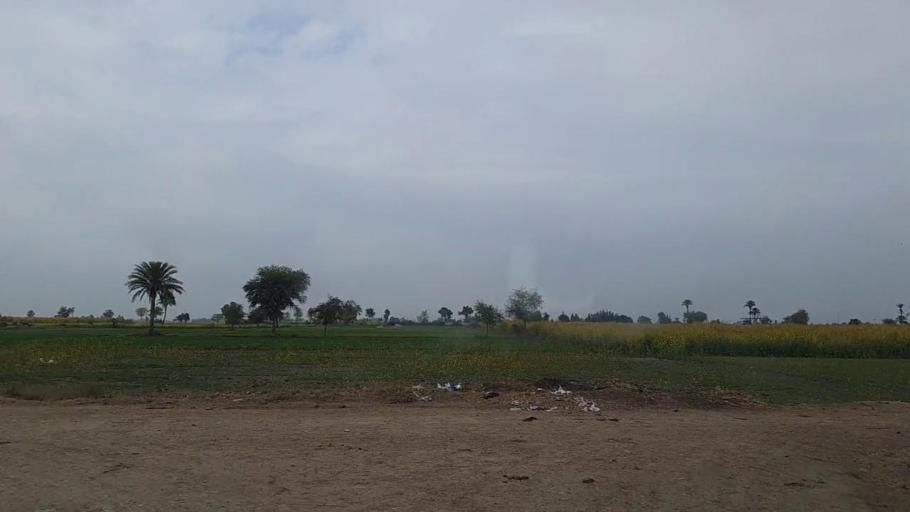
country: PK
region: Sindh
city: Sanghar
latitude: 26.1071
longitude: 68.9553
